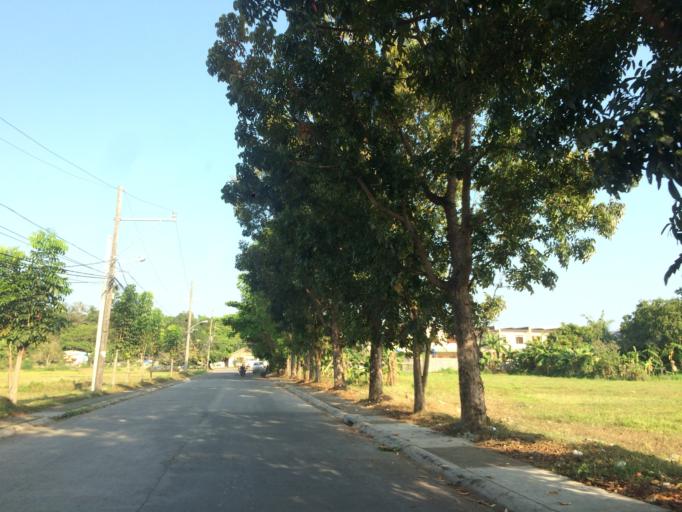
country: PH
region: Calabarzon
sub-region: Province of Rizal
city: San Mateo
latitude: 14.6731
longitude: 121.1221
